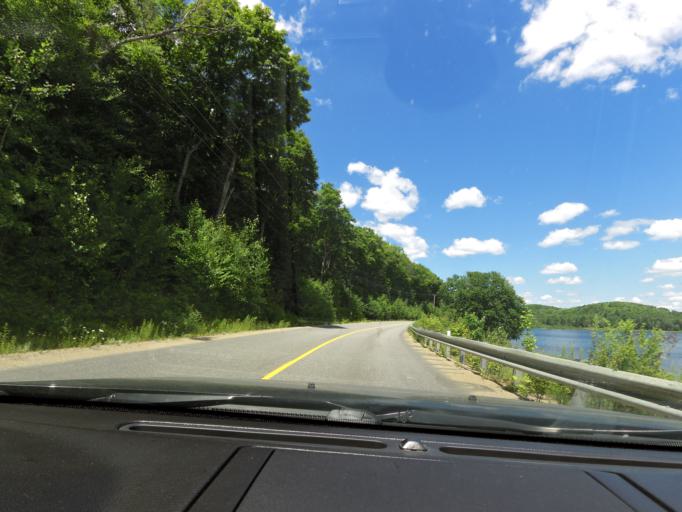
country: CA
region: Ontario
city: Huntsville
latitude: 45.5820
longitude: -79.2164
